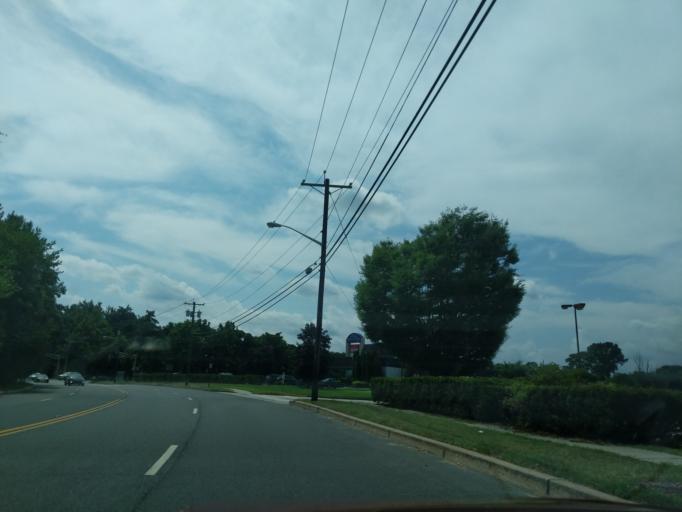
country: US
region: New Jersey
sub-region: Camden County
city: Glendora
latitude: 39.8314
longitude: -75.1088
